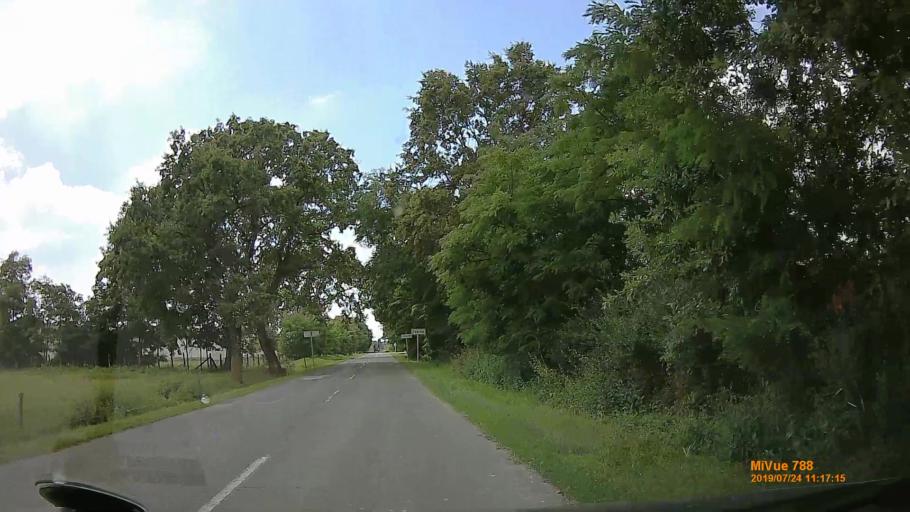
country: HU
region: Szabolcs-Szatmar-Bereg
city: Tarpa
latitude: 48.1719
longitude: 22.4612
